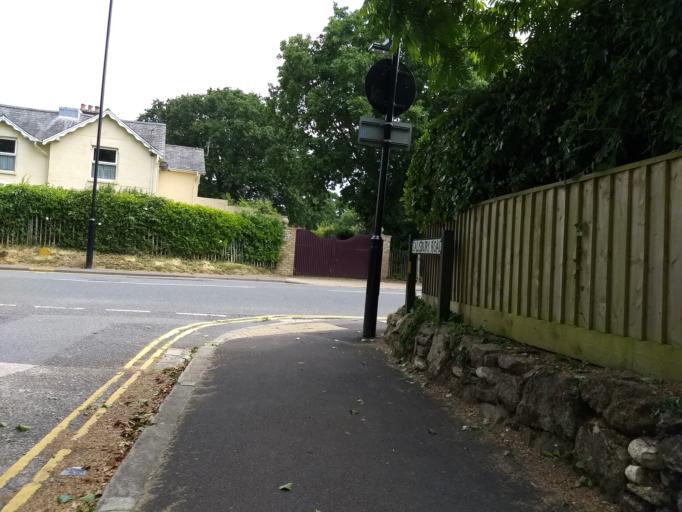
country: GB
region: England
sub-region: Isle of Wight
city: Ryde
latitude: 50.7172
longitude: -1.1470
